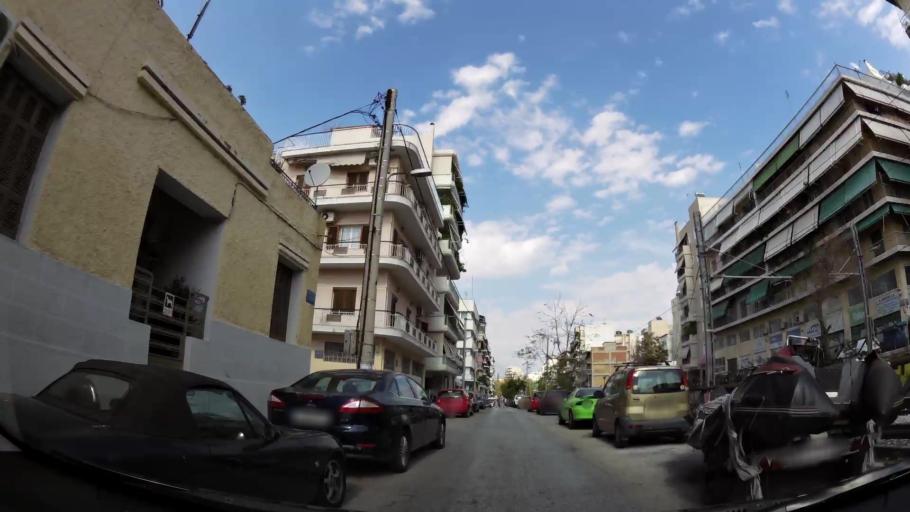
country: GR
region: Attica
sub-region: Nomarchia Athinas
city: Kipseli
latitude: 38.0037
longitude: 23.7209
